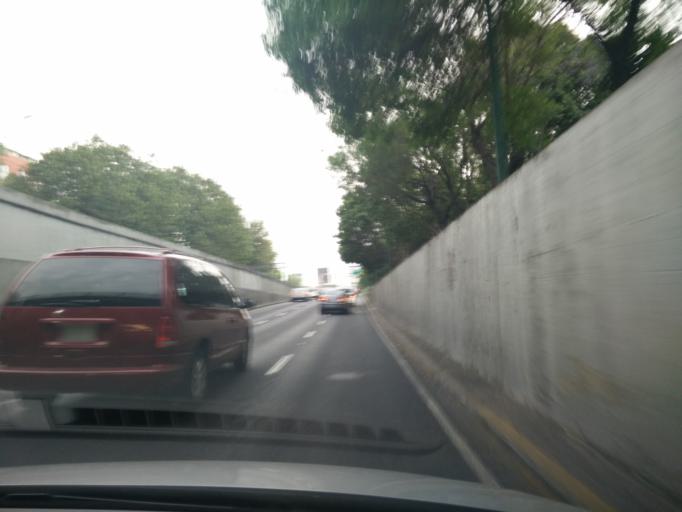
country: MX
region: Mexico City
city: Colonia Nativitas
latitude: 19.4032
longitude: -99.1337
